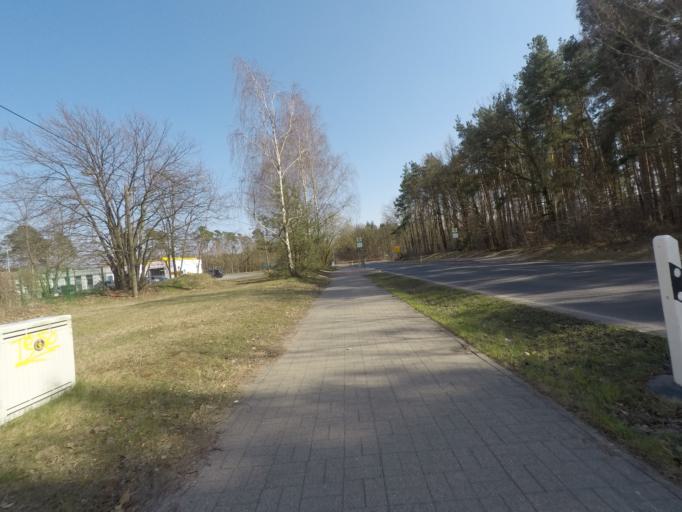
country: DE
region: Brandenburg
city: Eberswalde
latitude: 52.8475
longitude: 13.7884
